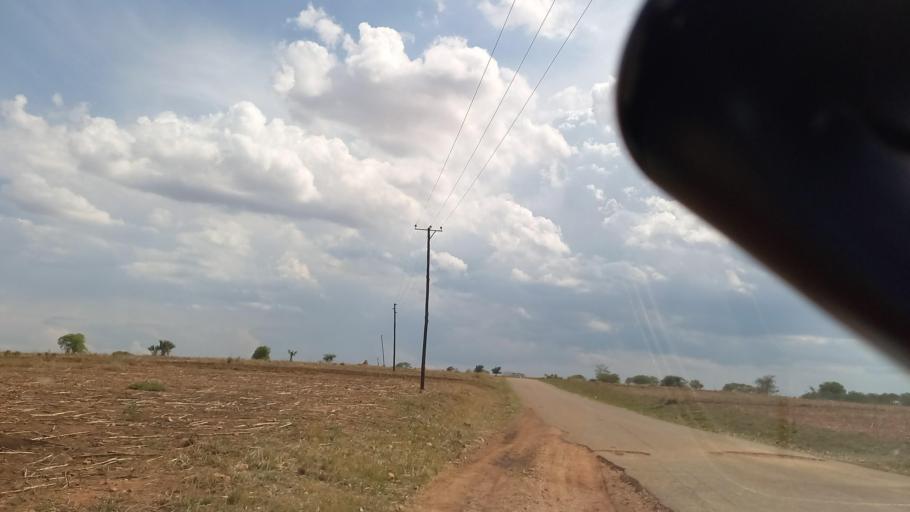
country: ZM
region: Lusaka
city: Kafue
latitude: -16.1822
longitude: 28.0877
